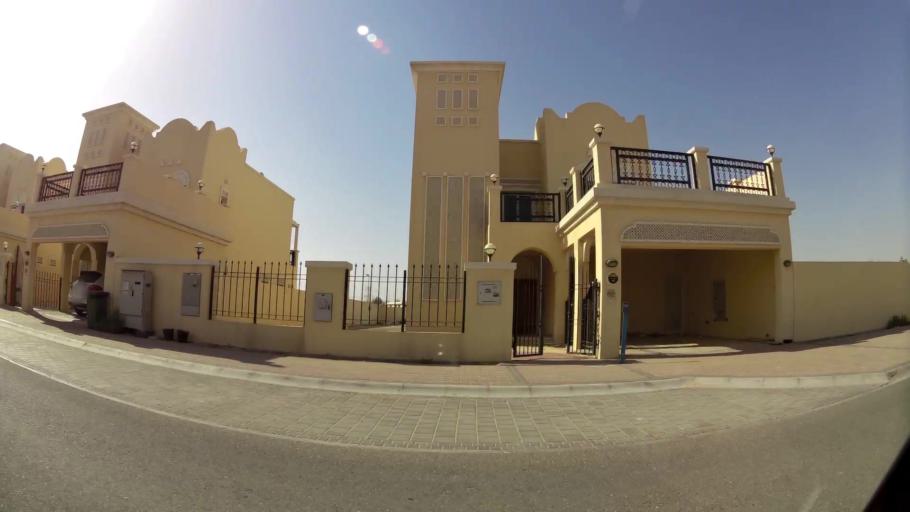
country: AE
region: Dubai
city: Dubai
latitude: 25.0717
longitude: 55.2132
